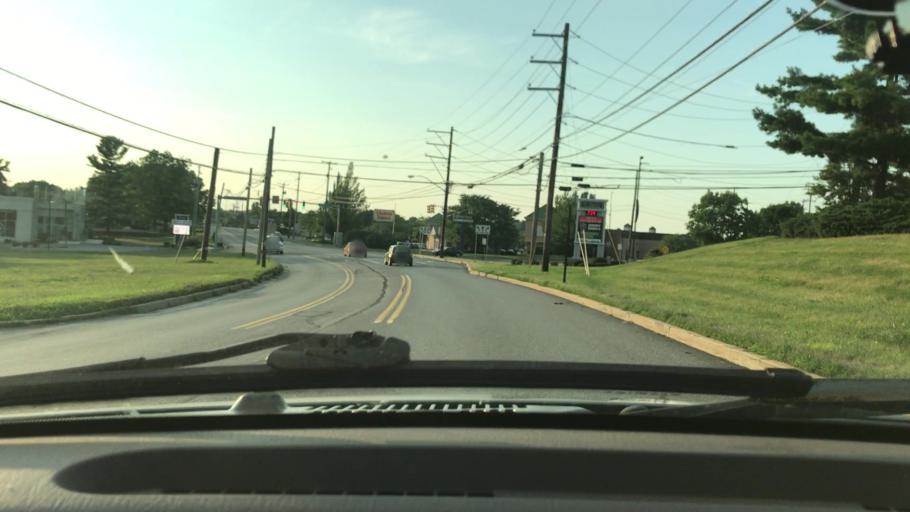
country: US
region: Pennsylvania
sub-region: Lancaster County
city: East Petersburg
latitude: 40.0807
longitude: -76.3394
